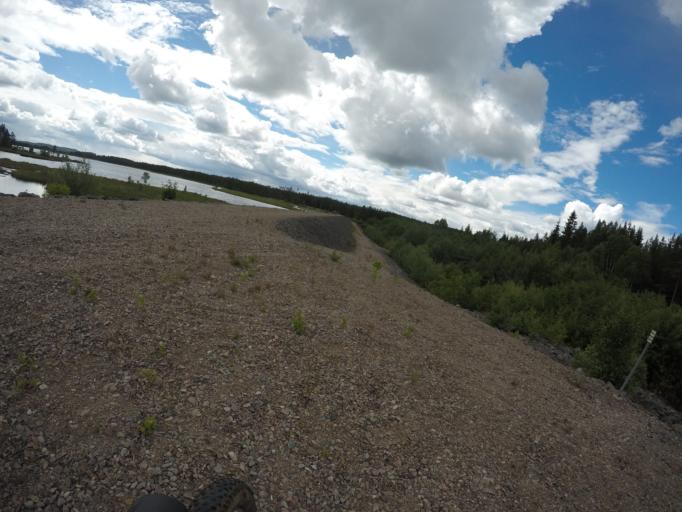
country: SE
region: Vaermland
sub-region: Filipstads Kommun
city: Lesjofors
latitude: 60.1457
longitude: 14.2396
